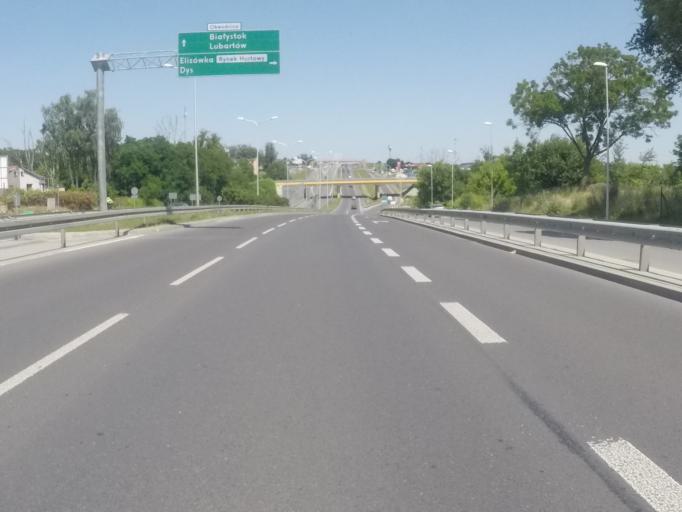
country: PL
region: Lublin Voivodeship
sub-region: Powiat lubelski
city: Lublin
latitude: 51.2840
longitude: 22.5761
